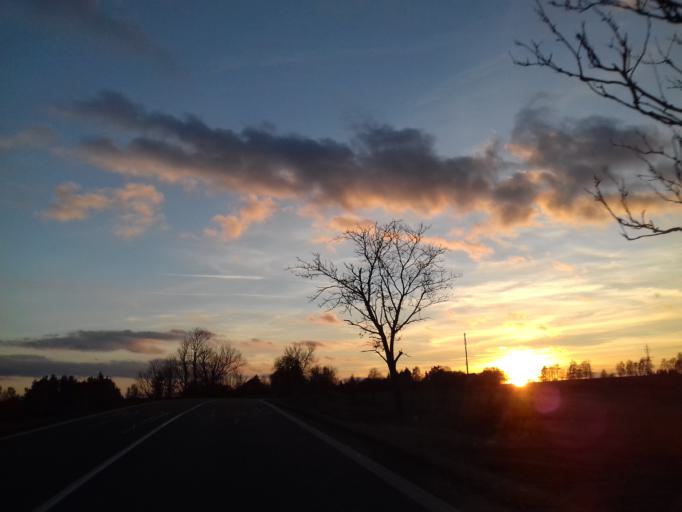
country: CZ
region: Vysocina
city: Krizova
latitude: 49.7130
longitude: 15.8527
